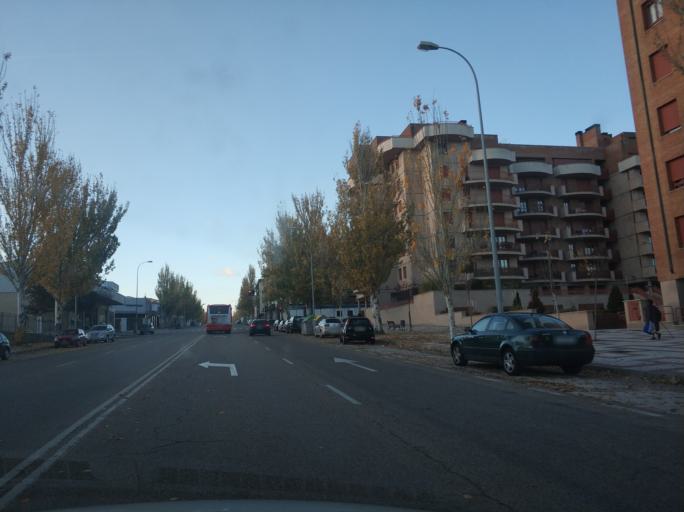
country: ES
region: Castille and Leon
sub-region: Provincia de Soria
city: Soria
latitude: 41.7582
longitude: -2.4740
